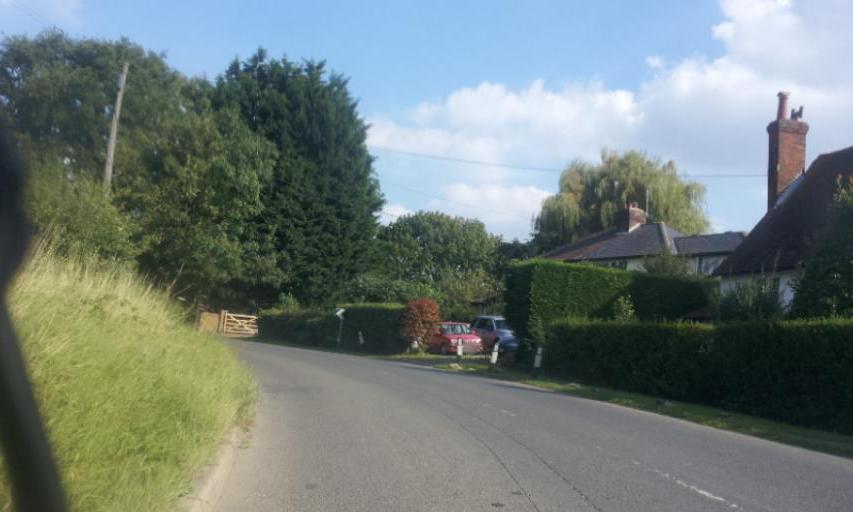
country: GB
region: England
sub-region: Kent
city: Yalding
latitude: 51.2165
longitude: 0.4547
